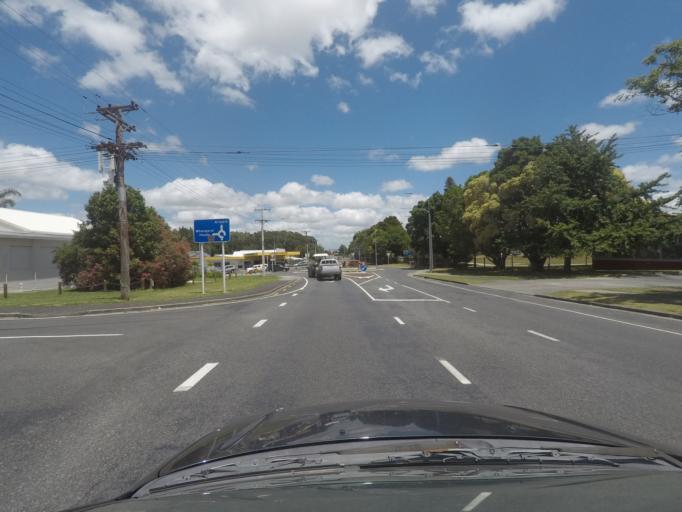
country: NZ
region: Northland
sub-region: Whangarei
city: Whangarei
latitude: -35.7566
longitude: 174.3683
